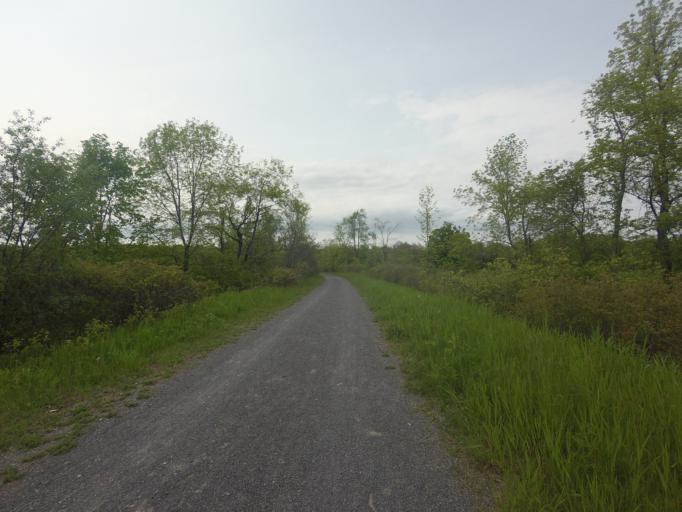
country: CA
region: Ontario
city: Kingston
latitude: 44.3022
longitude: -76.5588
